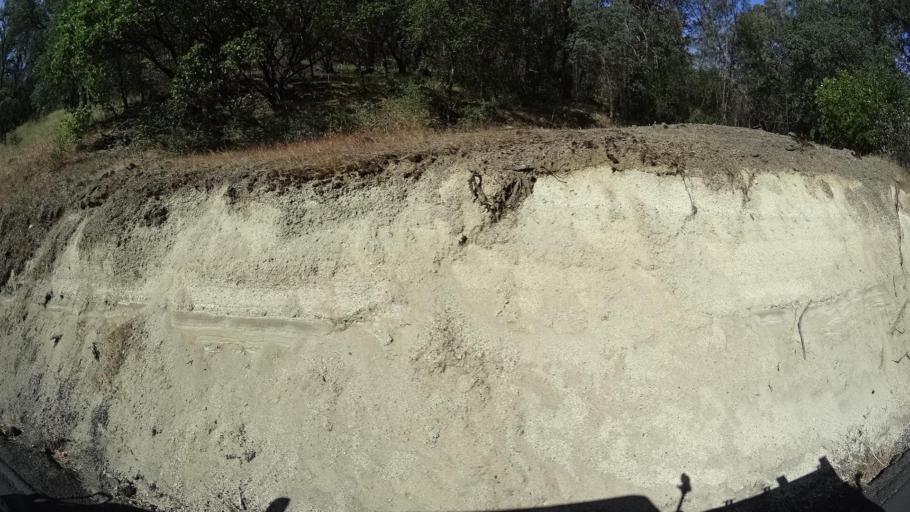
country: US
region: California
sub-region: Lake County
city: Kelseyville
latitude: 38.9611
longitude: -122.8275
